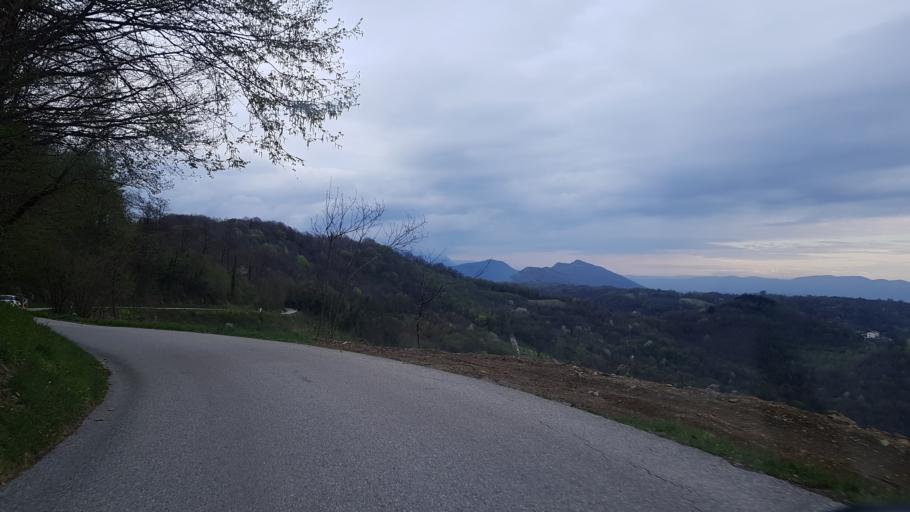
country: SI
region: Kanal
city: Deskle
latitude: 46.0344
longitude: 13.5659
